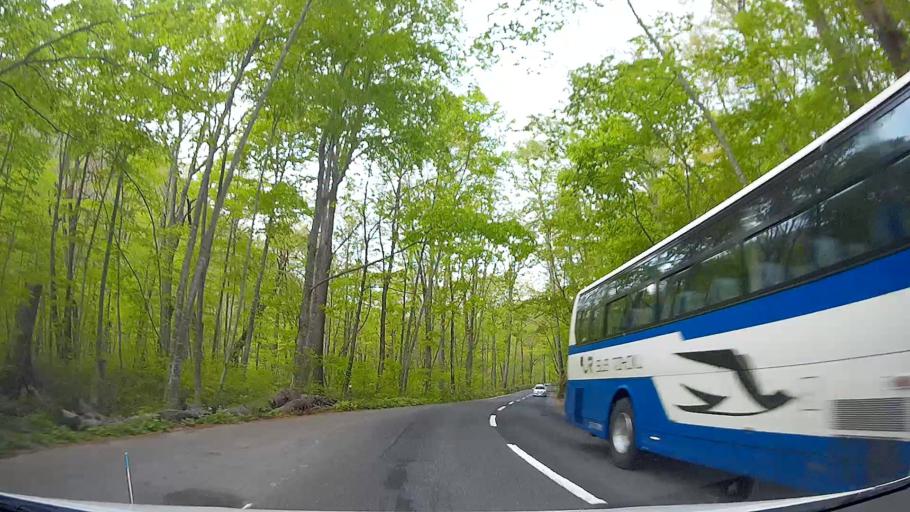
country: JP
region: Aomori
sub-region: Aomori Shi
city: Furudate
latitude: 40.5660
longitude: 140.9744
